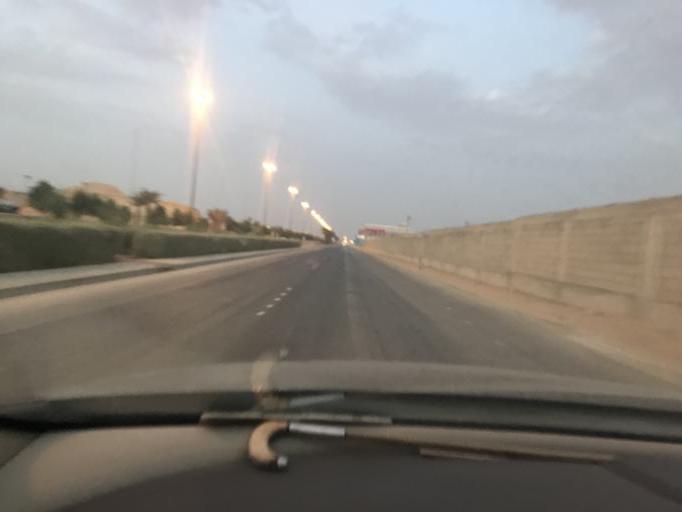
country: SA
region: Ar Riyad
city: Riyadh
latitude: 24.8462
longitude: 46.6618
